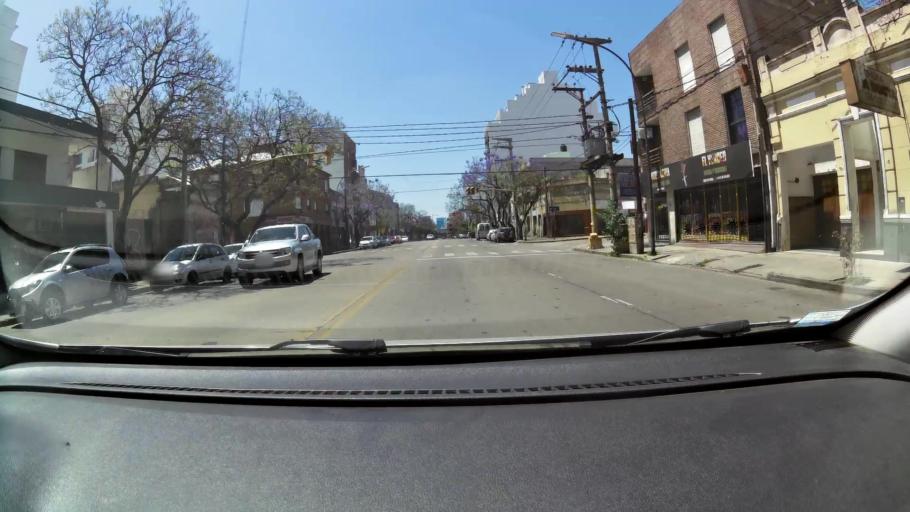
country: AR
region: Cordoba
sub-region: Departamento de Capital
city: Cordoba
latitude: -31.4028
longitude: -64.1984
